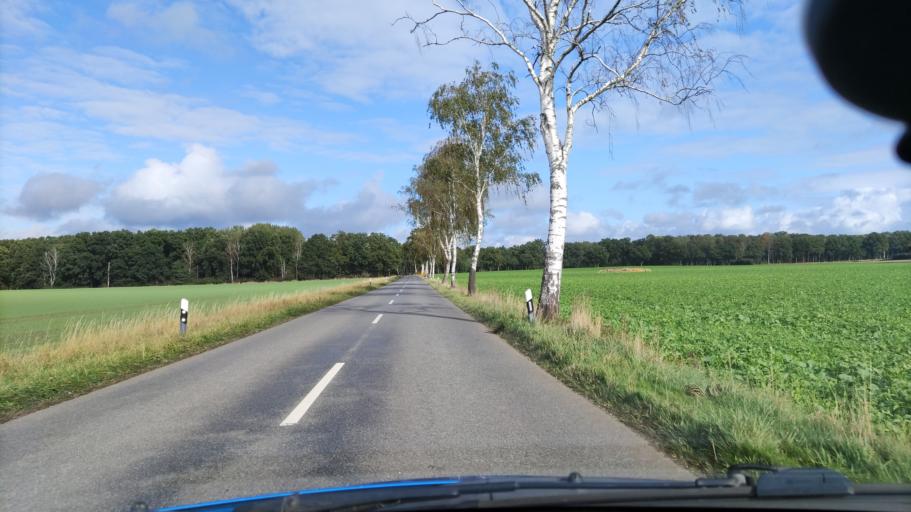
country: DE
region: Lower Saxony
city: Romstedt
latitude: 53.0890
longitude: 10.6745
